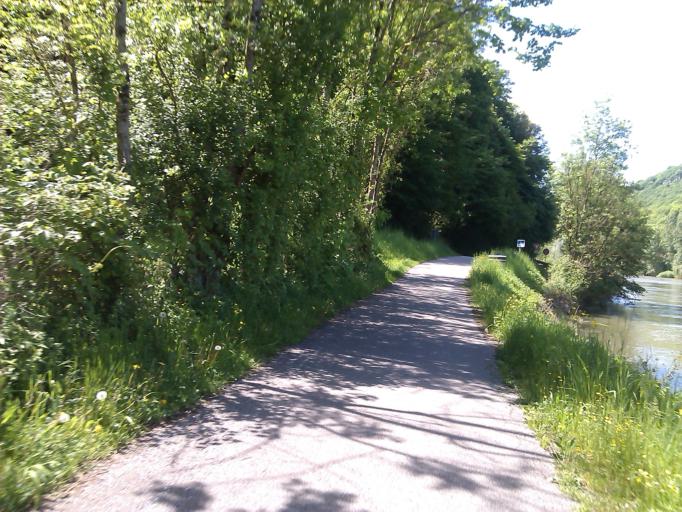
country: FR
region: Franche-Comte
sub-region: Departement du Doubs
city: Avanne-Aveney
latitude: 47.1981
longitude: 5.9835
